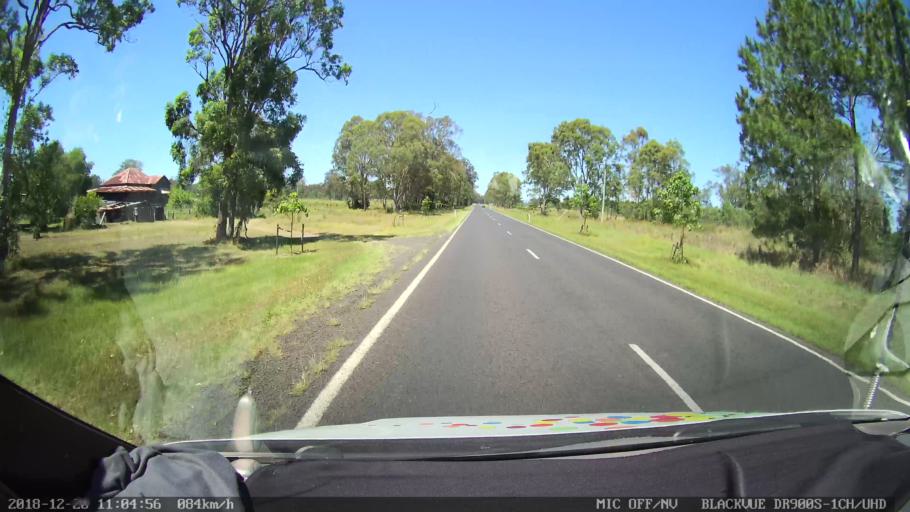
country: AU
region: New South Wales
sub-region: Richmond Valley
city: Casino
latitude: -28.8910
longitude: 153.0455
